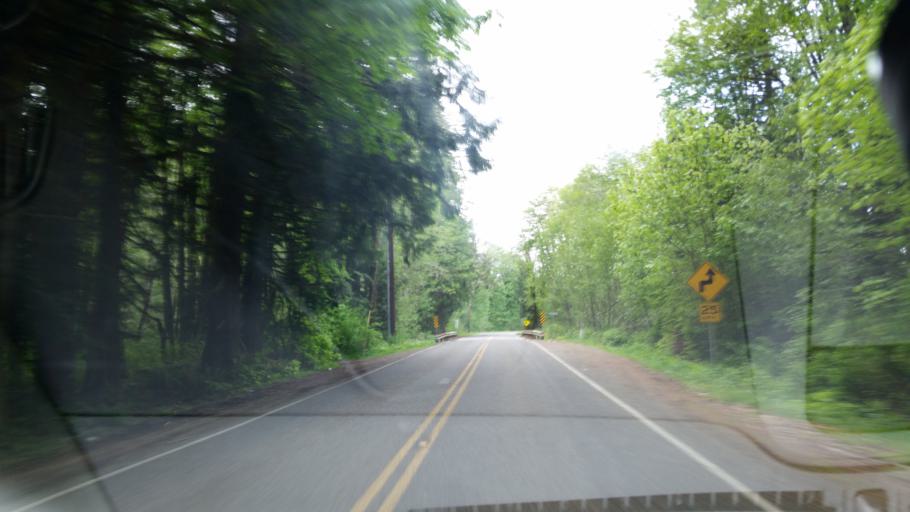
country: US
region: Washington
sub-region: Mason County
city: Shelton
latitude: 47.3157
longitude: -123.2546
